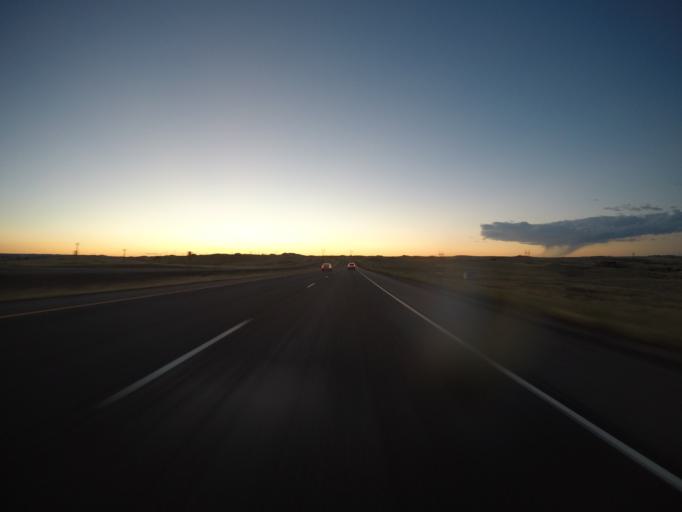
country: US
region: Wyoming
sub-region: Albany County
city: Laramie
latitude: 41.0310
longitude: -105.4376
